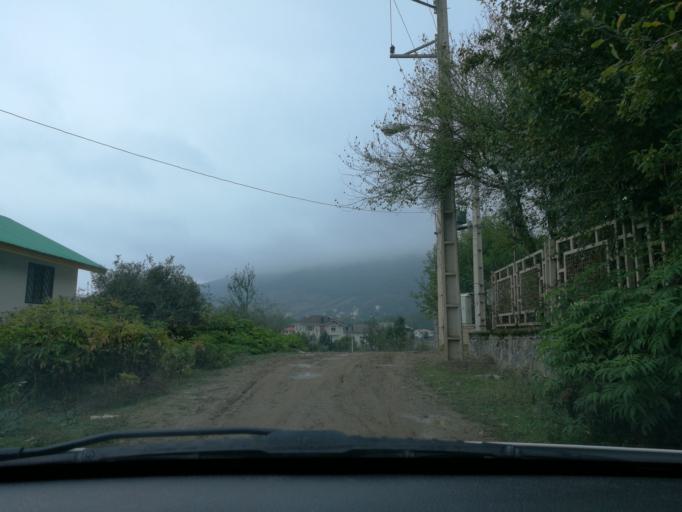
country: IR
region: Mazandaran
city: `Abbasabad
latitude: 36.5020
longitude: 51.2078
